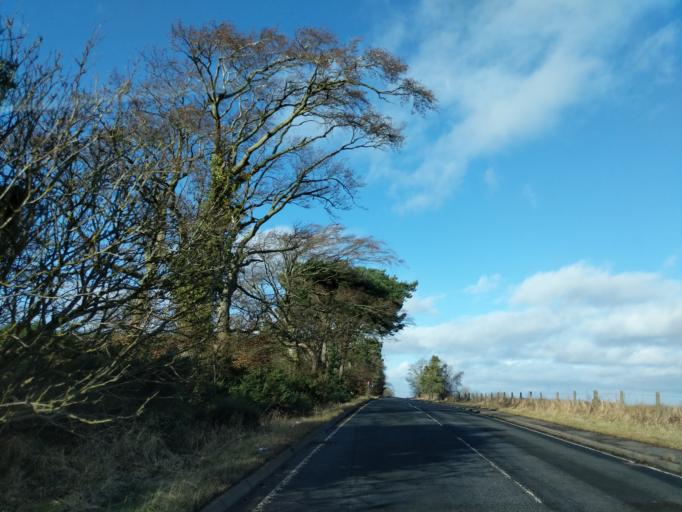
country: GB
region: Scotland
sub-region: West Lothian
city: Kirknewton
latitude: 55.8713
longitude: -3.4064
